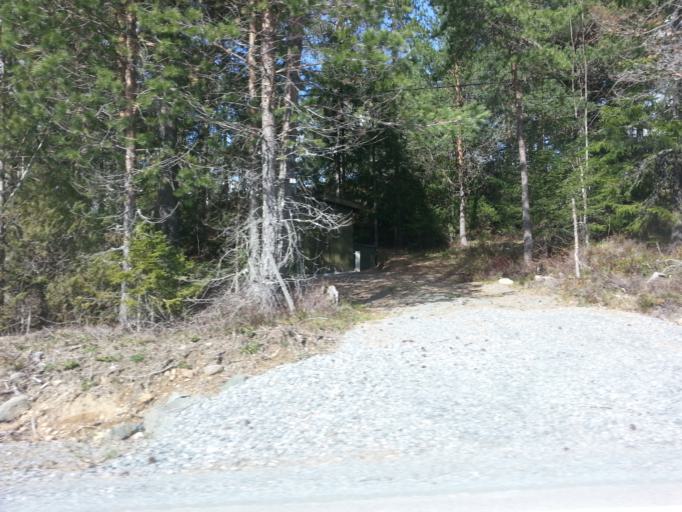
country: NO
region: Nord-Trondelag
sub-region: Levanger
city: Skogn
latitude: 63.6108
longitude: 11.1347
